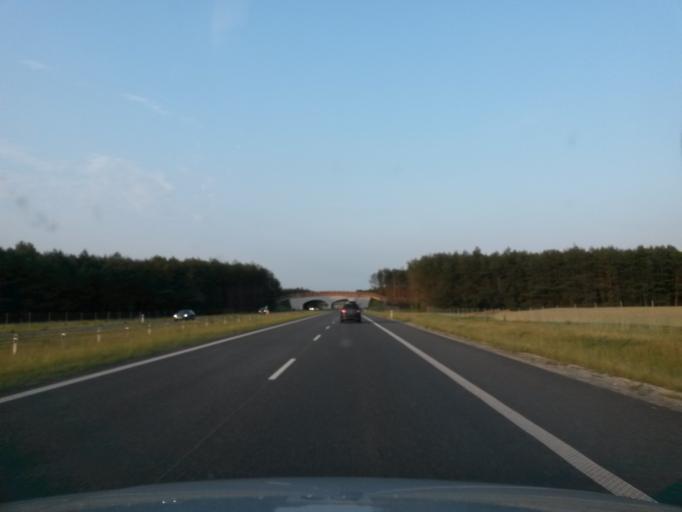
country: PL
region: Lodz Voivodeship
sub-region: Powiat wieruszowski
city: Galewice
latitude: 51.3069
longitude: 18.2237
